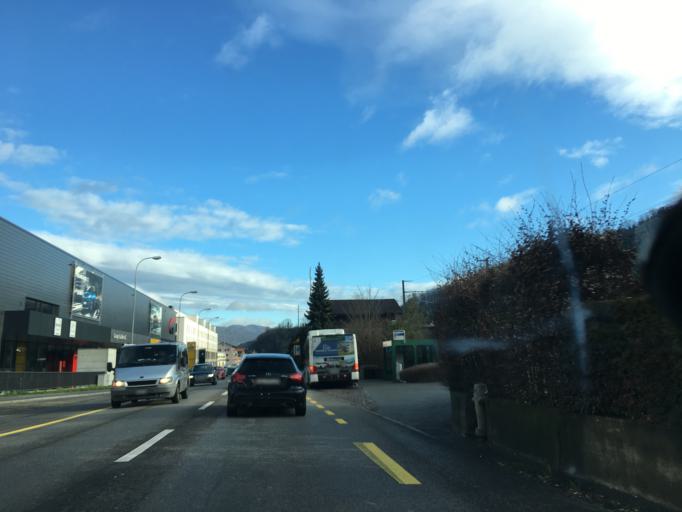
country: CH
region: Aargau
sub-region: Bezirk Zofingen
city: Aarburg
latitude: 47.3328
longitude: 7.9062
